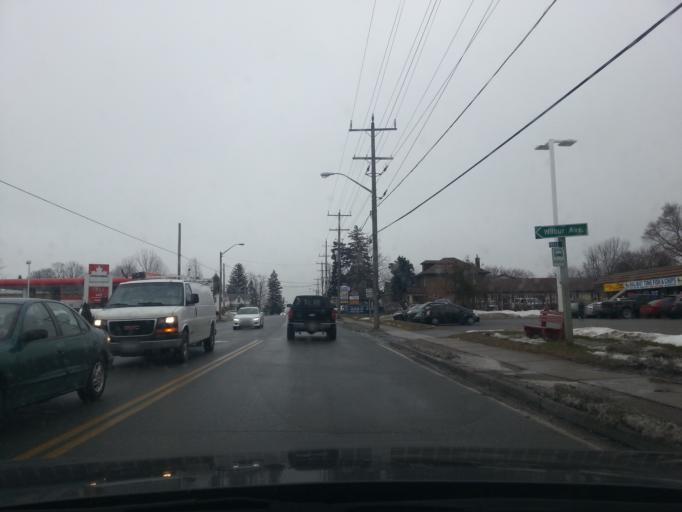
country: CA
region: Ontario
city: Uxbridge
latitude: 44.0999
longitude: -78.9450
